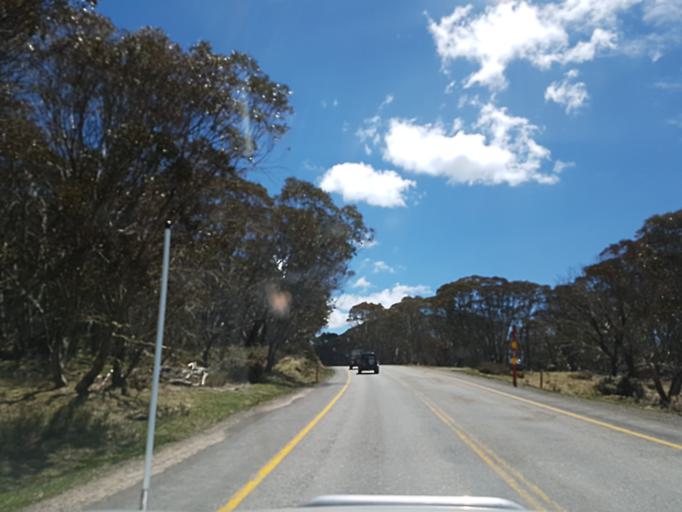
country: AU
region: Victoria
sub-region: Alpine
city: Mount Beauty
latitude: -37.0114
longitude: 147.1896
